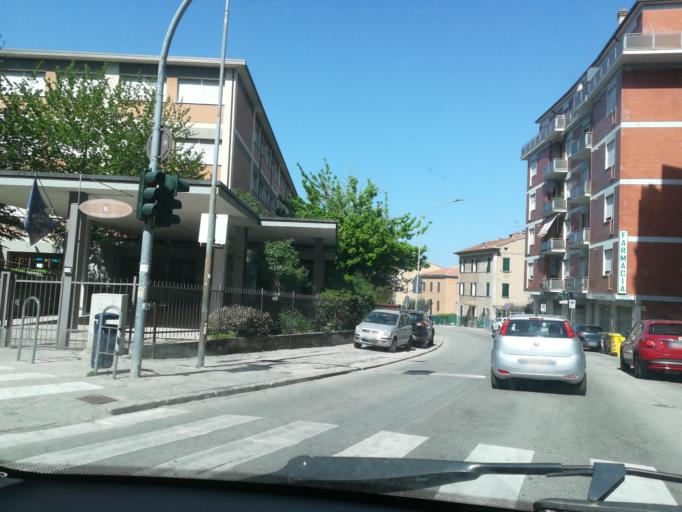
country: IT
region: The Marches
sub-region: Provincia di Macerata
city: Macerata
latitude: 43.3017
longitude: 13.4595
